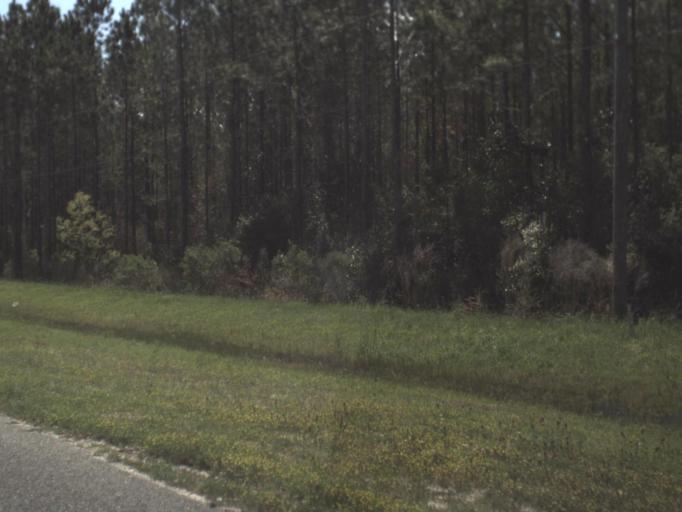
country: US
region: Florida
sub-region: Bay County
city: Laguna Beach
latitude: 30.3085
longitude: -85.8534
